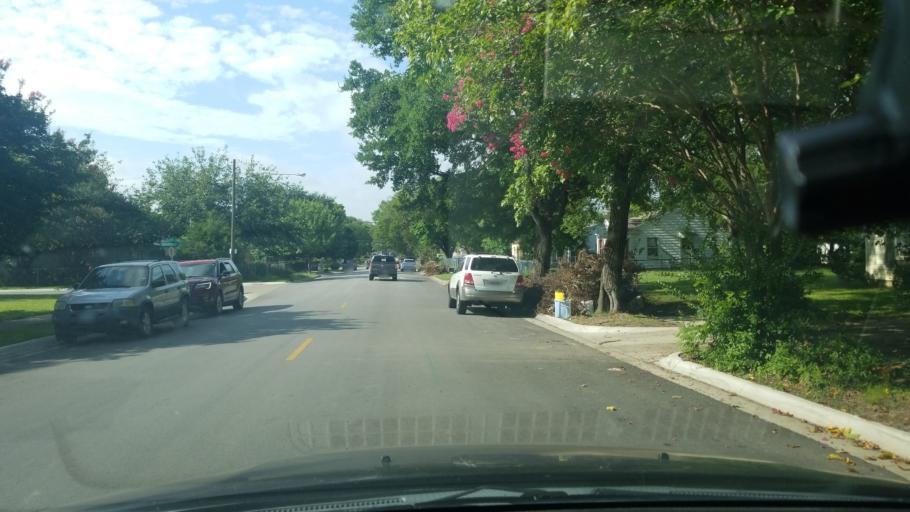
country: US
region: Texas
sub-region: Dallas County
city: Balch Springs
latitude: 32.7419
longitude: -96.6743
